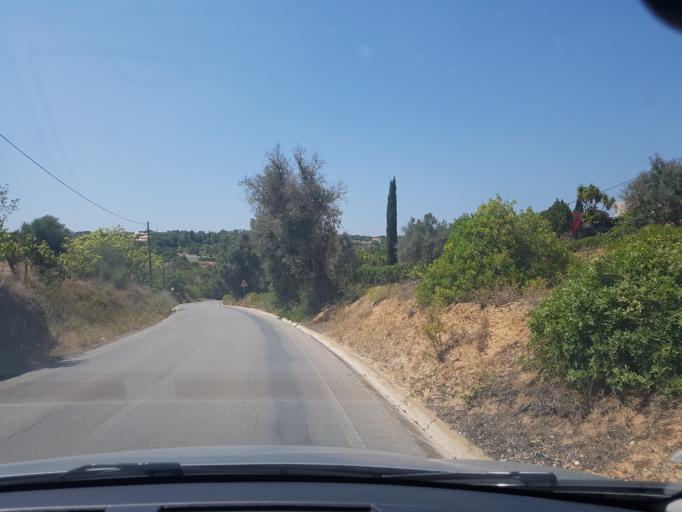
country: PT
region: Faro
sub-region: Lagoa
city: Carvoeiro
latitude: 37.1002
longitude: -8.4253
